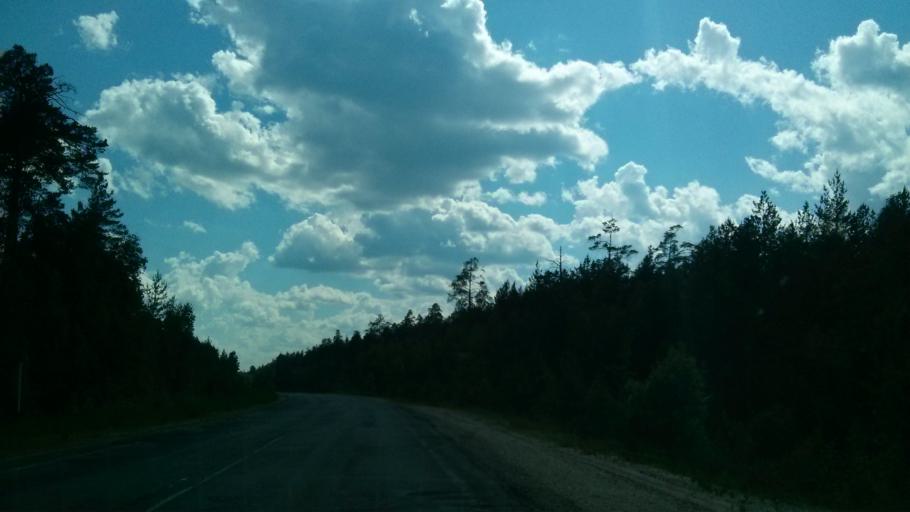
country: RU
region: Vladimir
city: Melenki
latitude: 55.3519
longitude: 41.6776
